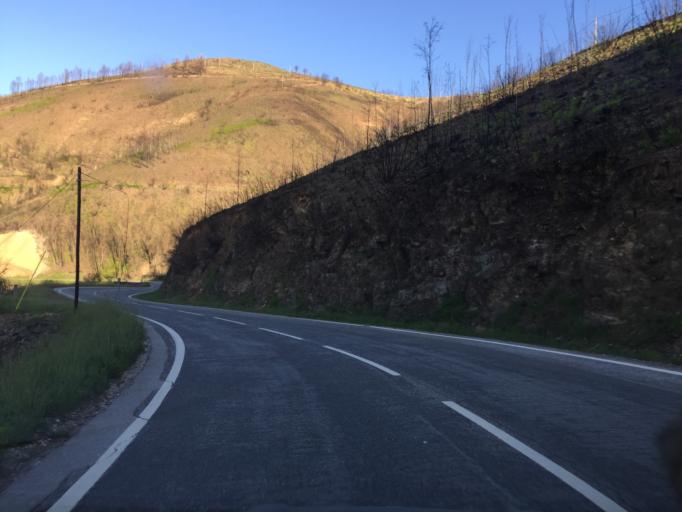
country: PT
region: Coimbra
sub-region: Pampilhosa da Serra
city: Pampilhosa da Serra
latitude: 40.0294
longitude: -7.9650
